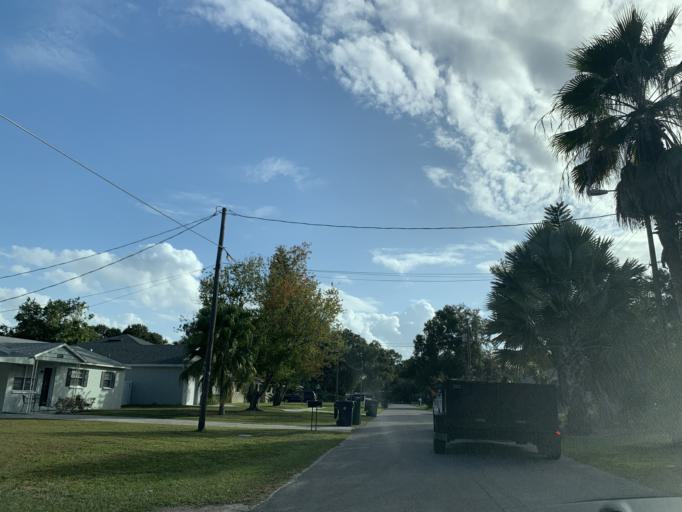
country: US
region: Florida
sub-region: Hillsborough County
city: Tampa
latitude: 27.9029
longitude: -82.5115
